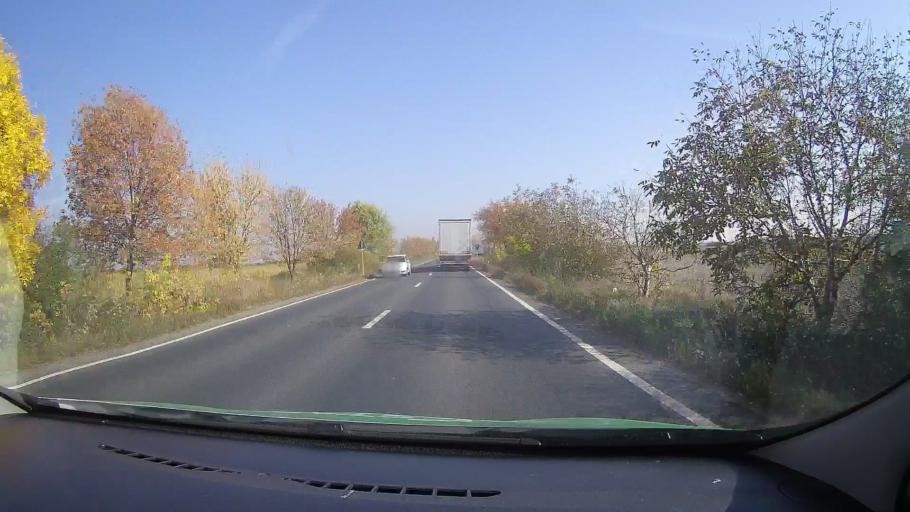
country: RO
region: Bihor
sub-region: Municipiul Salonta
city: Salonta
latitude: 46.7774
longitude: 21.6222
